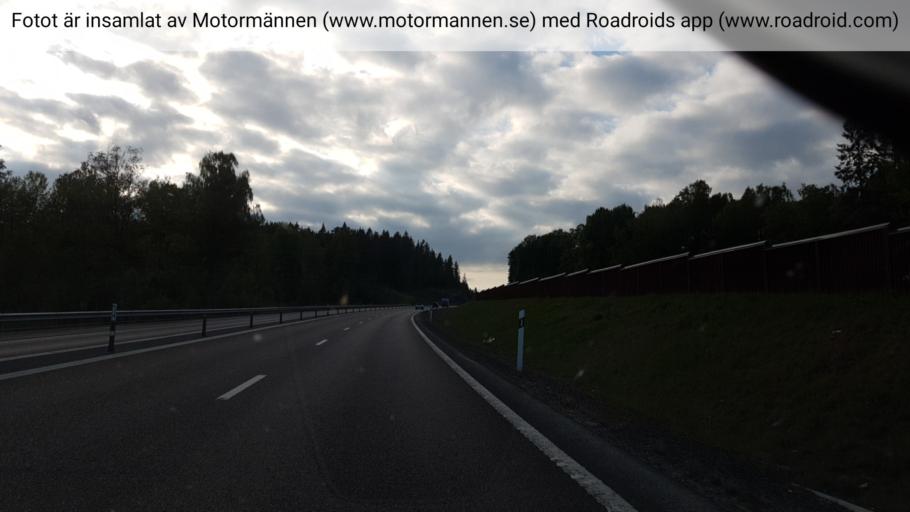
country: SE
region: Joenkoeping
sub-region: Jonkopings Kommun
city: Tenhult
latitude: 57.7228
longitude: 14.3553
